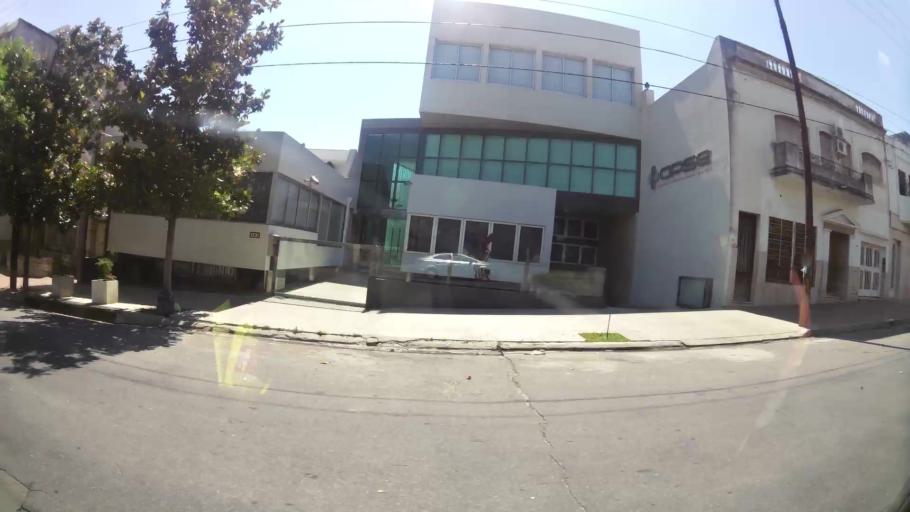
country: AR
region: Cordoba
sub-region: Departamento de Capital
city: Cordoba
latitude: -31.4024
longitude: -64.1821
